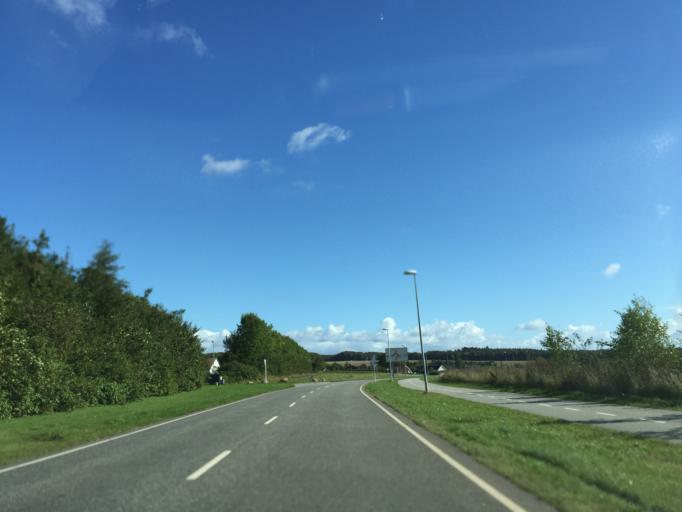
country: DK
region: Central Jutland
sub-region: Viborg Kommune
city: Bjerringbro
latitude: 56.3949
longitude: 9.6699
